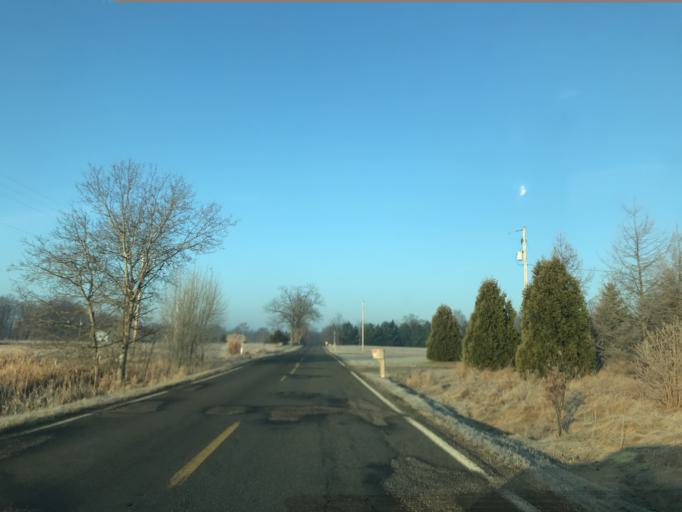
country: US
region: Michigan
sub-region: Ingham County
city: Leslie
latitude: 42.4011
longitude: -84.4765
